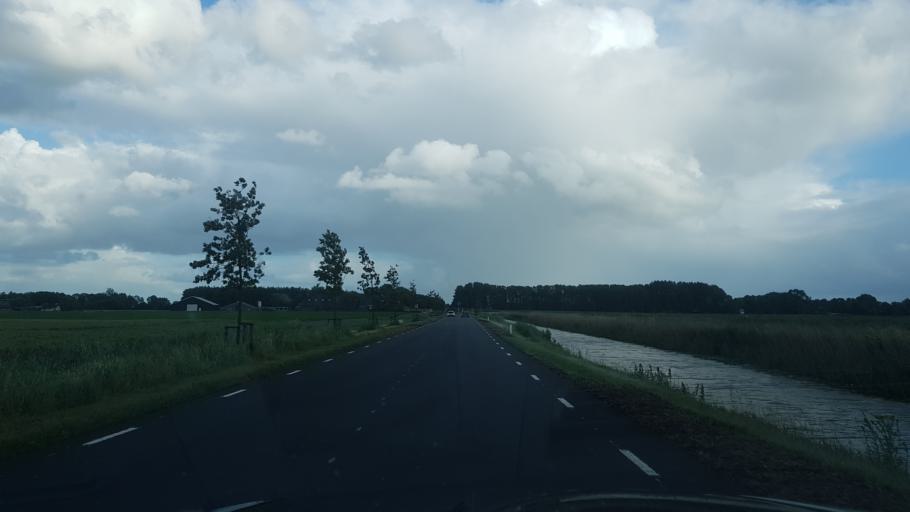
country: NL
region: Groningen
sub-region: Gemeente Appingedam
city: Appingedam
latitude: 53.3173
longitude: 6.7655
